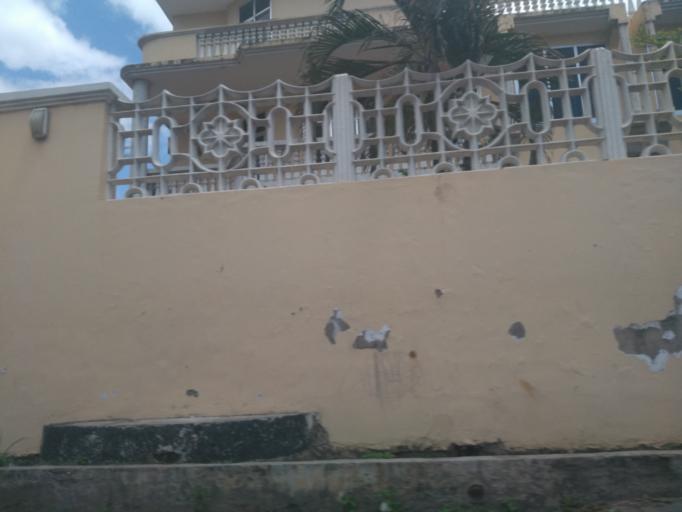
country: TZ
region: Dar es Salaam
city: Magomeni
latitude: -6.7946
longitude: 39.2685
